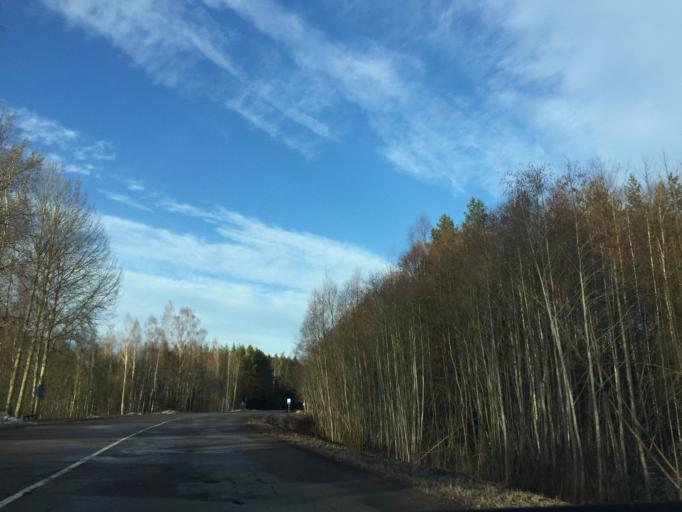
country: LV
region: Kekava
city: Balozi
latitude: 56.7502
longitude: 24.1072
